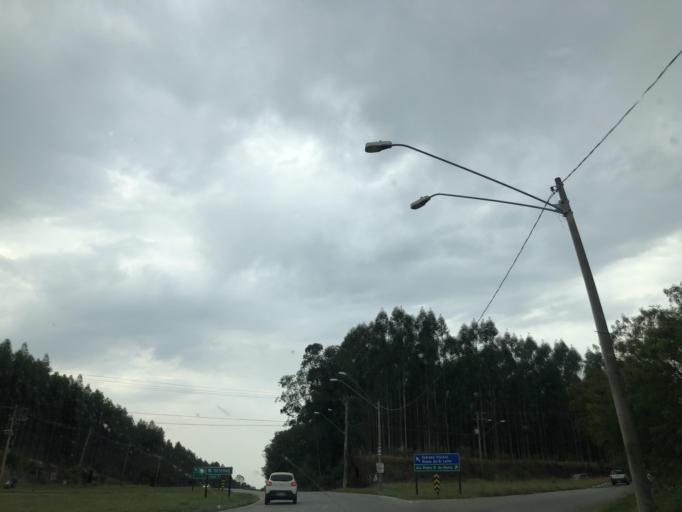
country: BR
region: Sao Paulo
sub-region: Salto De Pirapora
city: Salto de Pirapora
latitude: -23.6711
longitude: -47.6012
